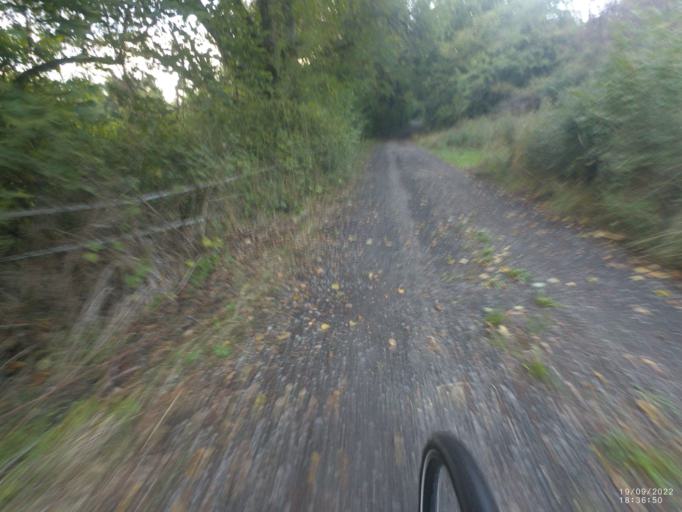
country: DE
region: Rheinland-Pfalz
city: Schalkenmehren
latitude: 50.1613
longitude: 6.8427
